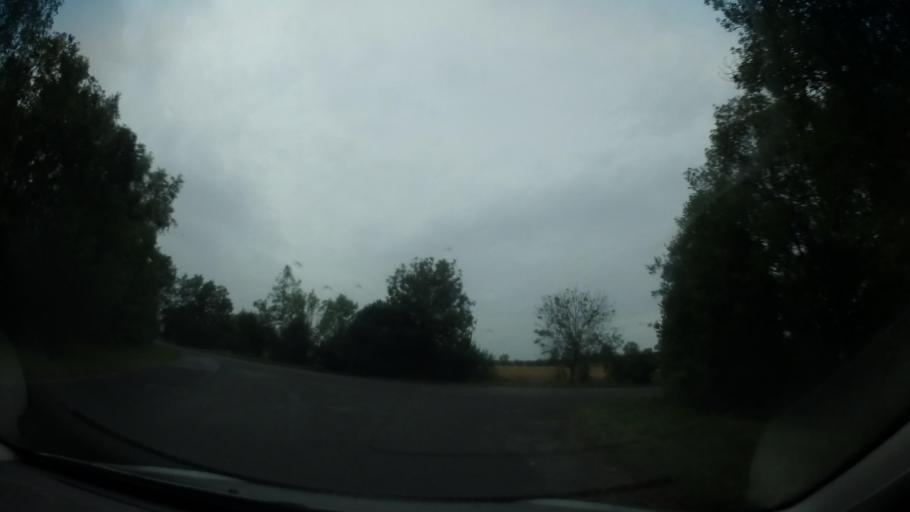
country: CZ
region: Central Bohemia
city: Milovice
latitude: 50.2420
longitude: 14.8972
